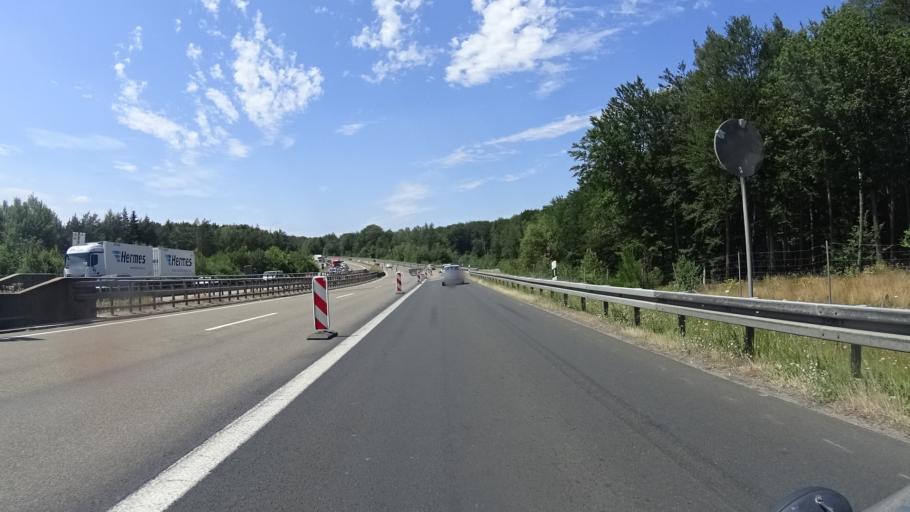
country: DE
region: Hesse
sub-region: Regierungsbezirk Kassel
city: Kirchheim
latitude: 50.8077
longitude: 9.5182
